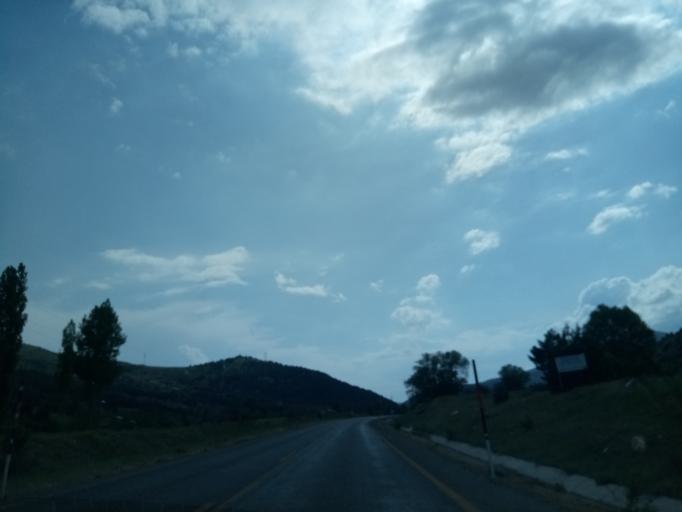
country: TR
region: Konya
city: Aksehir
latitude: 38.2730
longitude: 31.4160
